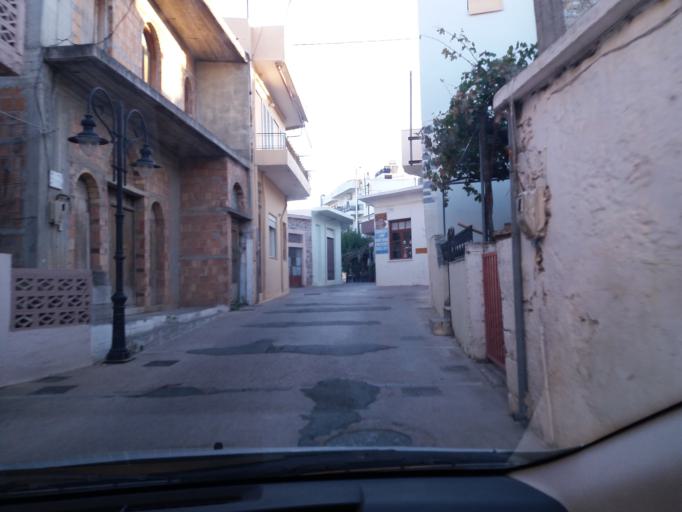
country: GR
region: Crete
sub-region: Nomos Irakleiou
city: Mokhos
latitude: 35.2643
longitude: 25.4229
